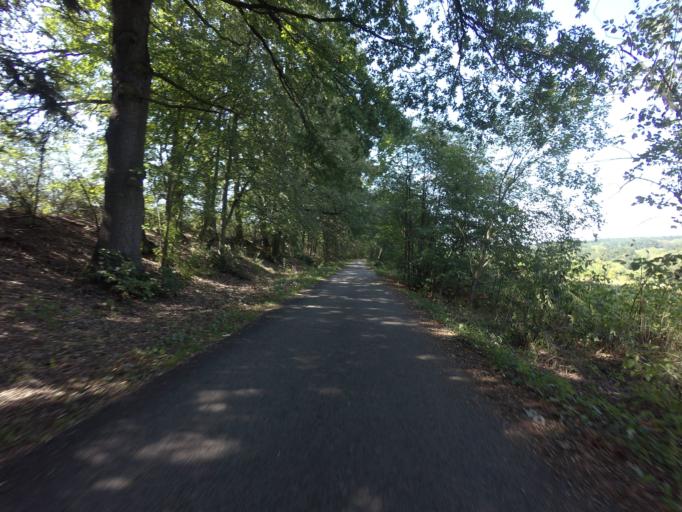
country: CZ
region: Jihocesky
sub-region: Okres Ceske Budejovice
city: Hluboka nad Vltavou
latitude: 49.1215
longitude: 14.4573
